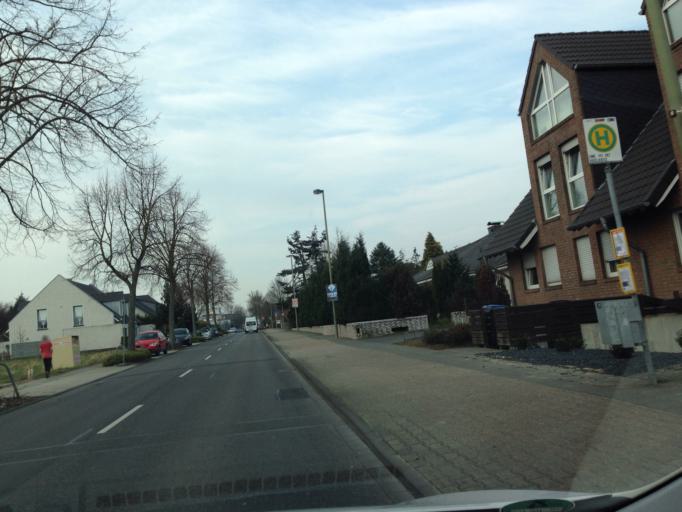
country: DE
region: North Rhine-Westphalia
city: Erkelenz
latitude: 51.0717
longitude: 6.3146
